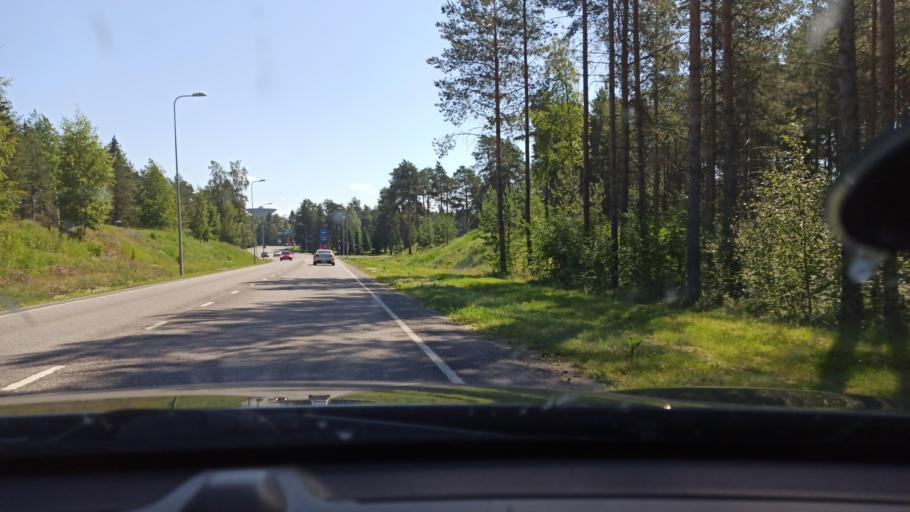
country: FI
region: Northern Ostrobothnia
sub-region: Oulu
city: Oulu
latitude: 65.0397
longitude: 25.4620
